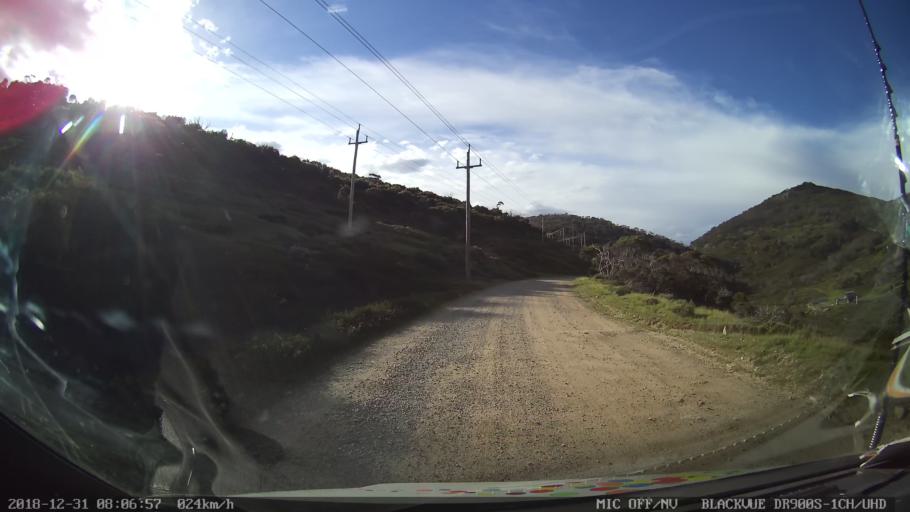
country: AU
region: New South Wales
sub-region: Snowy River
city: Jindabyne
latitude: -36.3763
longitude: 148.4086
